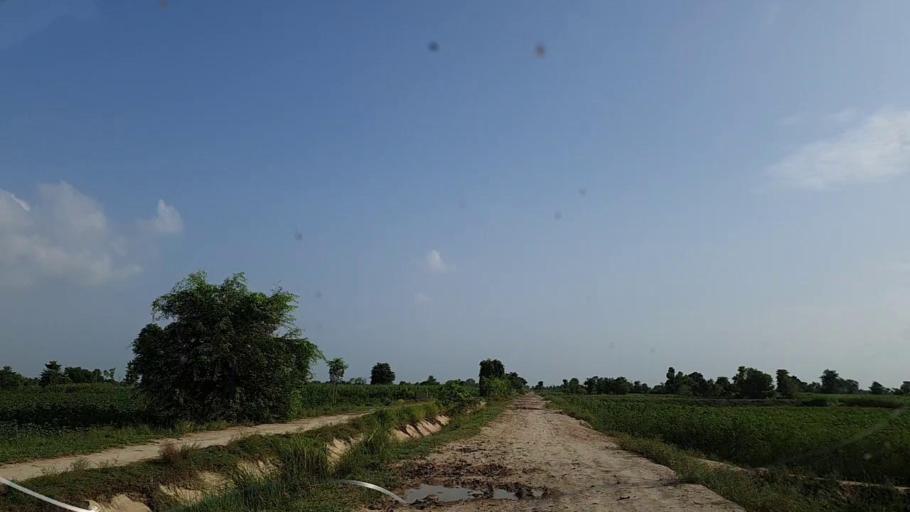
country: PK
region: Sindh
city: Bhiria
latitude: 26.8606
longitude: 68.2514
